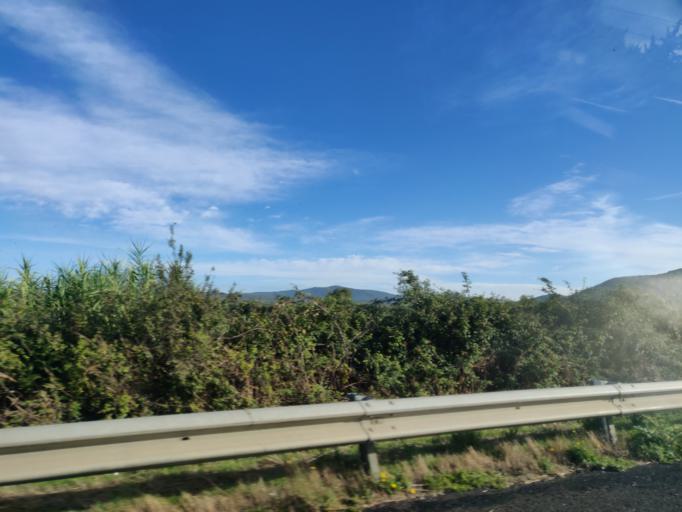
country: IT
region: Tuscany
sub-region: Provincia di Grosseto
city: Bagno Roselle
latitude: 42.7965
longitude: 11.1169
